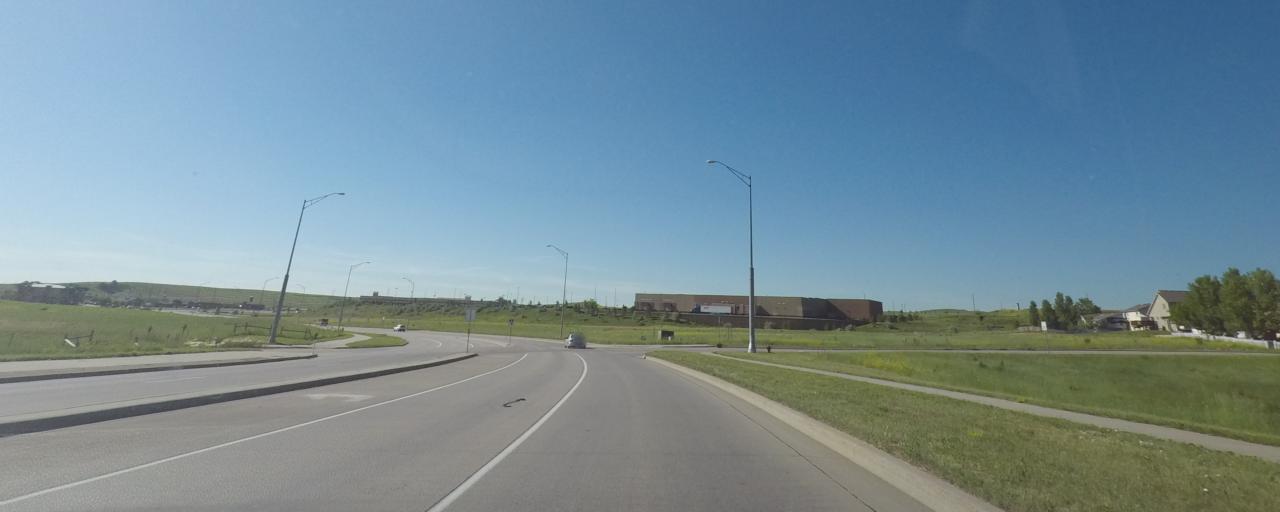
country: US
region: South Dakota
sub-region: Pennington County
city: Rapid City
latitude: 44.0376
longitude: -103.2191
